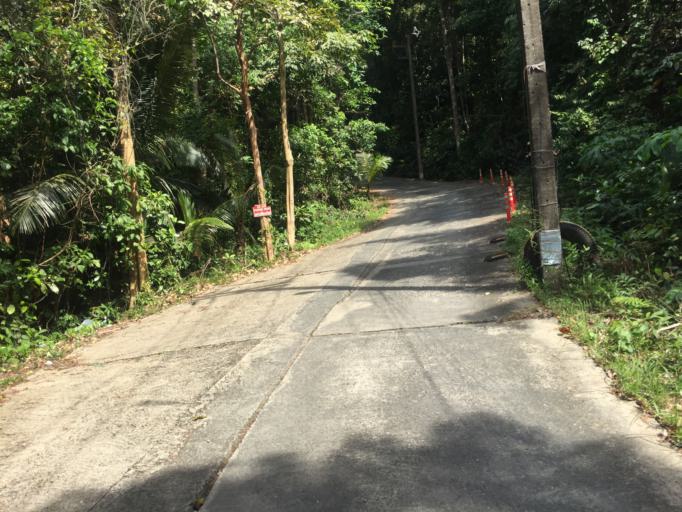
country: TH
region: Trat
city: Laem Ngop
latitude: 12.1169
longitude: 102.2664
